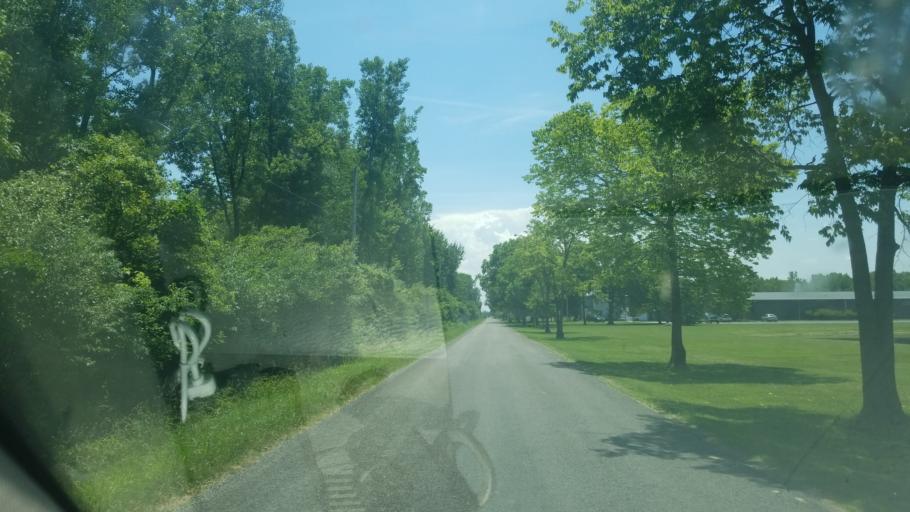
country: US
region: Ohio
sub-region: Hancock County
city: Findlay
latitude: 41.0069
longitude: -83.6362
